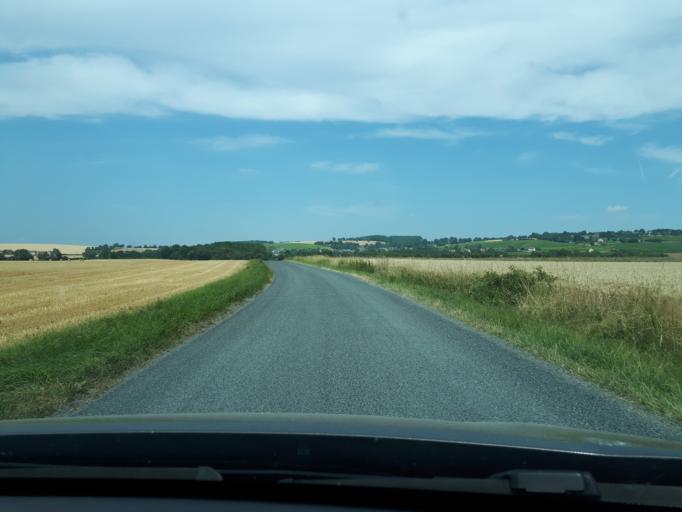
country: FR
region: Centre
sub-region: Departement du Cher
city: Sancerre
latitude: 47.2927
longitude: 2.7544
